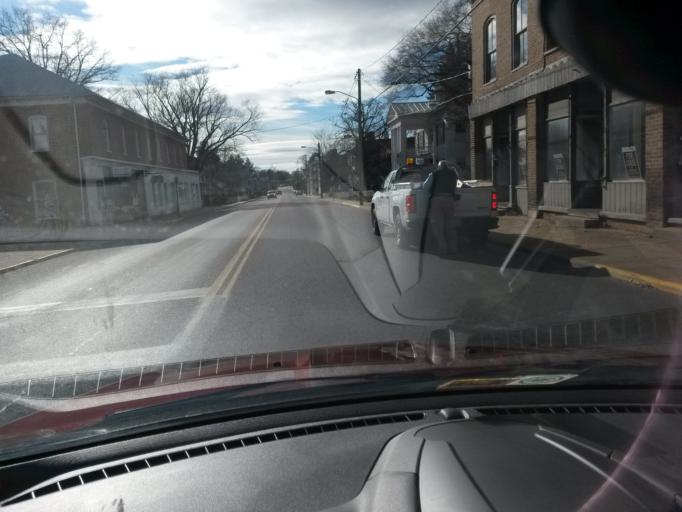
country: US
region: Virginia
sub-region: Rockingham County
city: Bridgewater
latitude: 38.3821
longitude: -78.9768
